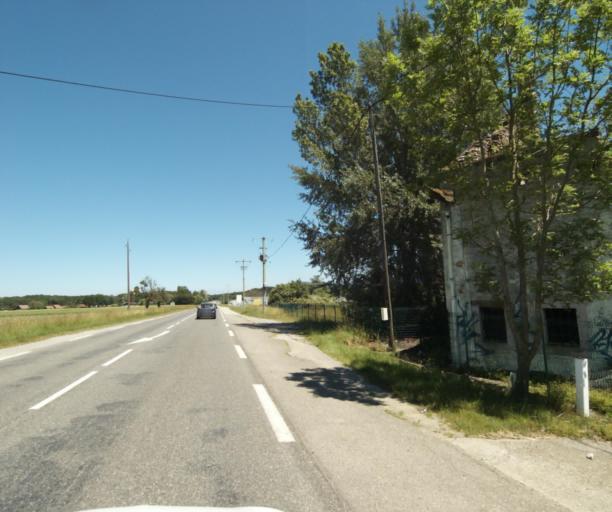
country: FR
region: Rhone-Alpes
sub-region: Departement de la Haute-Savoie
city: Veigy-Foncenex
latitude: 46.2806
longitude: 6.2529
